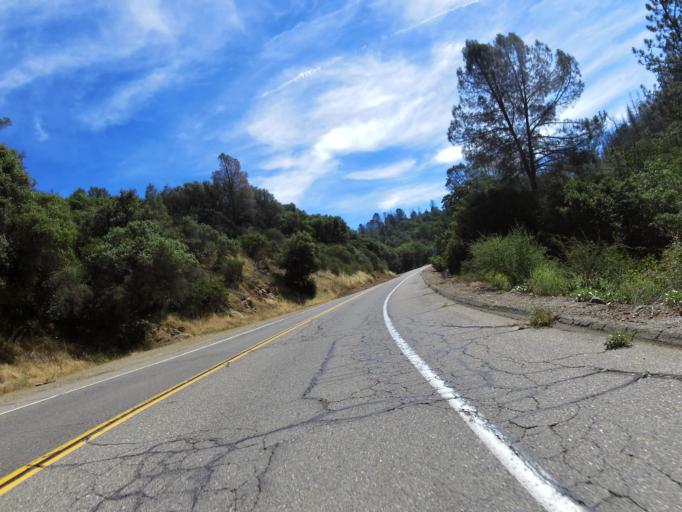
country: US
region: California
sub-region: Mariposa County
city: Mariposa
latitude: 37.5190
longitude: -119.9526
